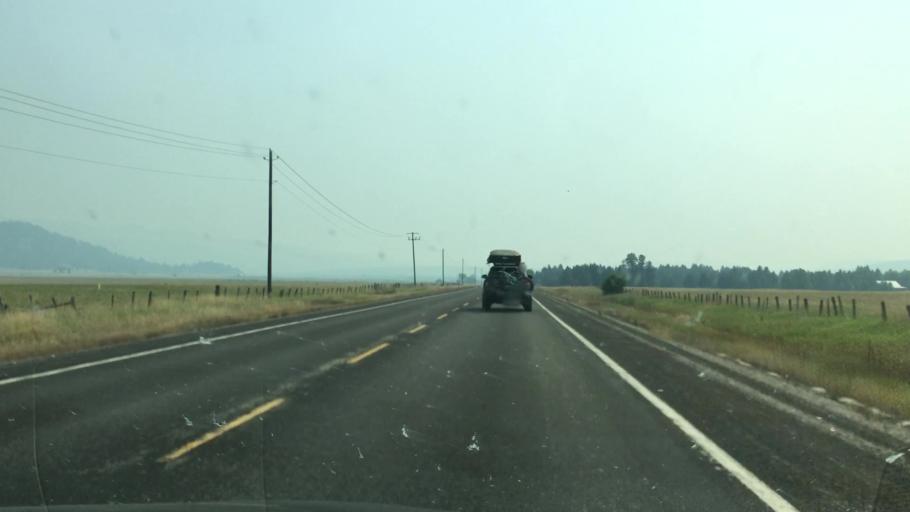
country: US
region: Idaho
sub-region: Valley County
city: Cascade
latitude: 44.4438
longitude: -115.9994
